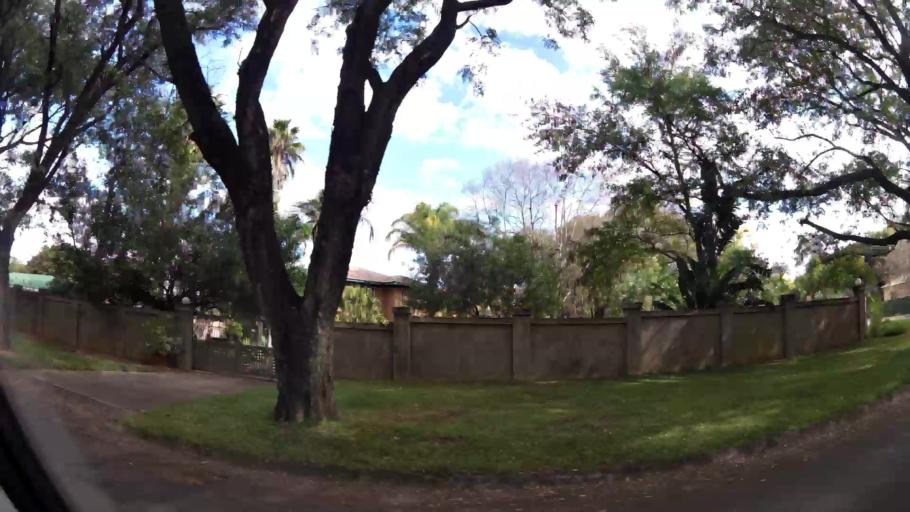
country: ZA
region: Limpopo
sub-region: Waterberg District Municipality
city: Modimolle
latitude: -24.7078
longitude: 28.4026
